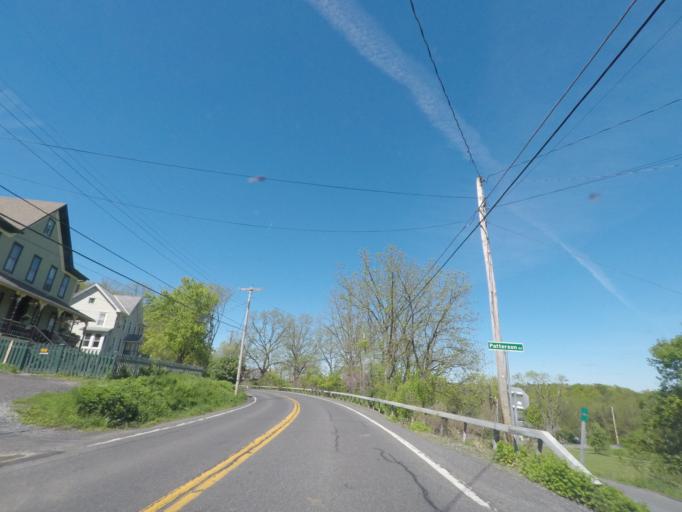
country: US
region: New York
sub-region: Ulster County
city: Saugerties
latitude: 42.1249
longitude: -73.9307
